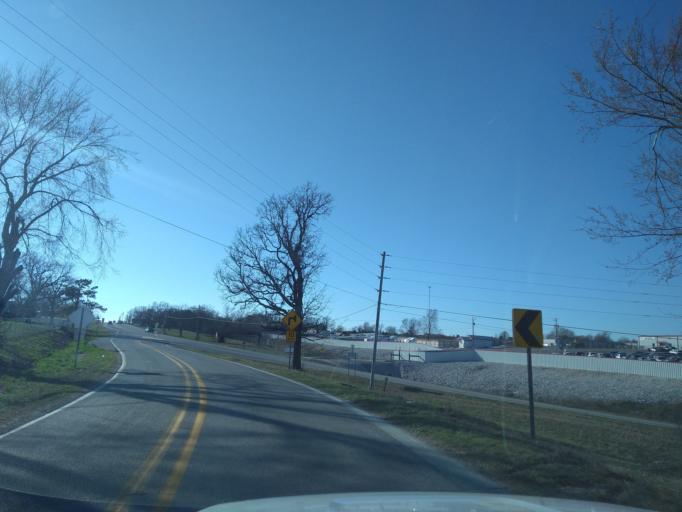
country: US
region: Arkansas
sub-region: Washington County
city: Lincoln
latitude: 35.9509
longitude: -94.3777
